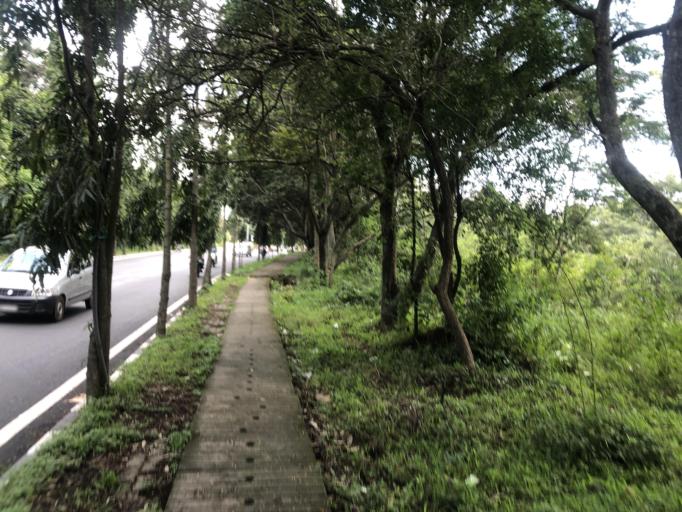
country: IN
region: Karnataka
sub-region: Bangalore Urban
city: Bangalore
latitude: 12.9375
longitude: 77.5111
